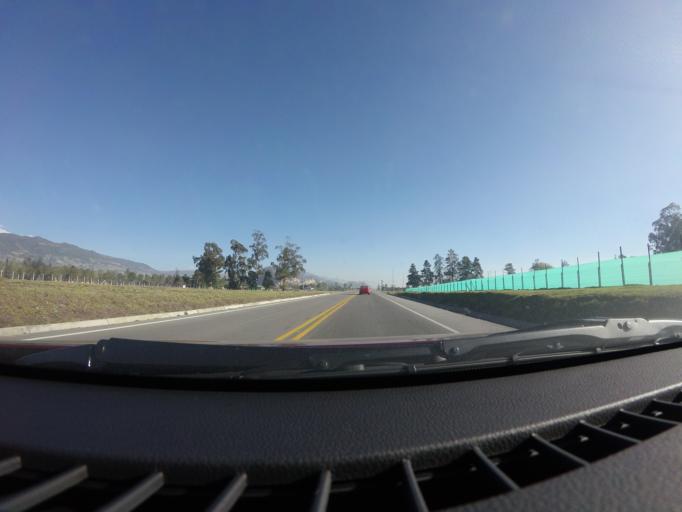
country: CO
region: Cundinamarca
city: Cogua
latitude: 5.0402
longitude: -73.9701
